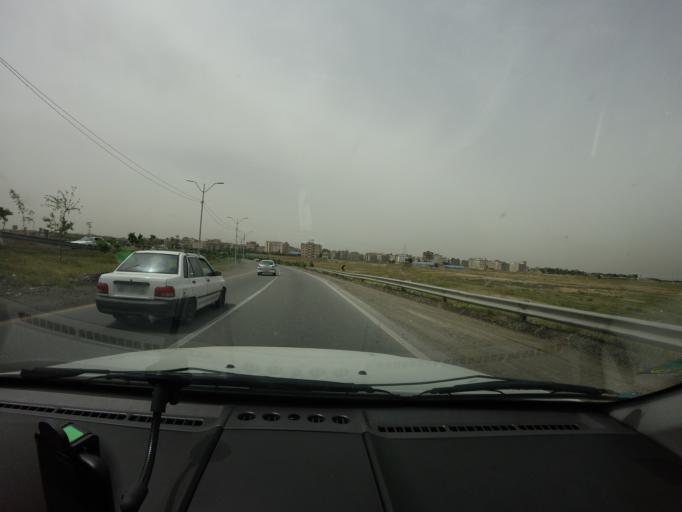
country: IR
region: Tehran
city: Eslamshahr
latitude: 35.5783
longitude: 51.2446
